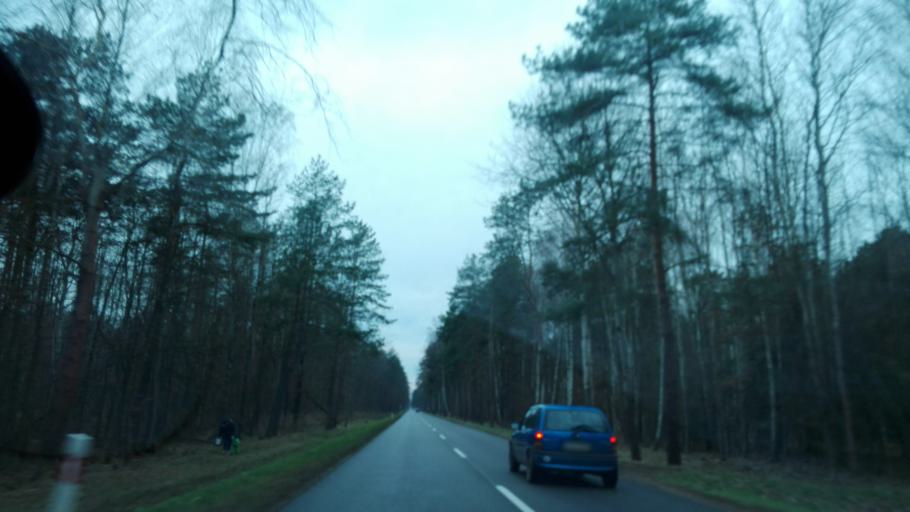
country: PL
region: Lublin Voivodeship
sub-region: Powiat radzynski
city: Komarowka Podlaska
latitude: 51.7769
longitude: 22.8963
